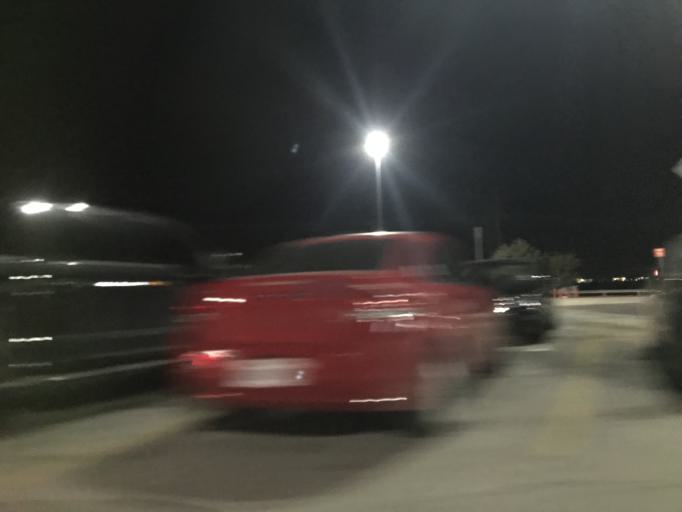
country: US
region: Texas
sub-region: Taylor County
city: Abilene
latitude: 32.4801
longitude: -99.6988
